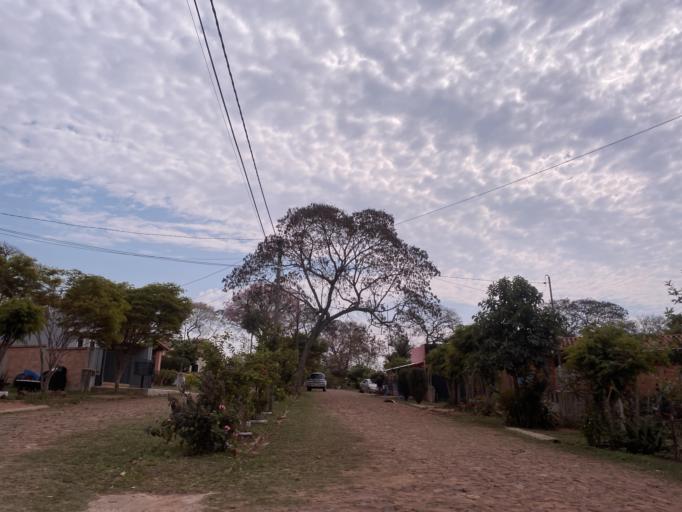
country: PY
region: Misiones
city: San Juan Bautista
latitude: -26.6785
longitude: -57.1372
